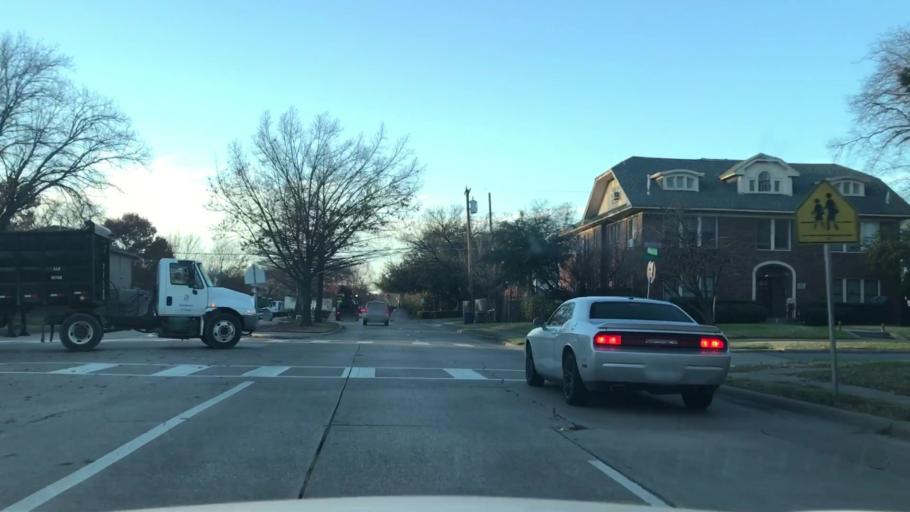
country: US
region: Texas
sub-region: Dallas County
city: Highland Park
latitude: 32.8013
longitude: -96.7639
